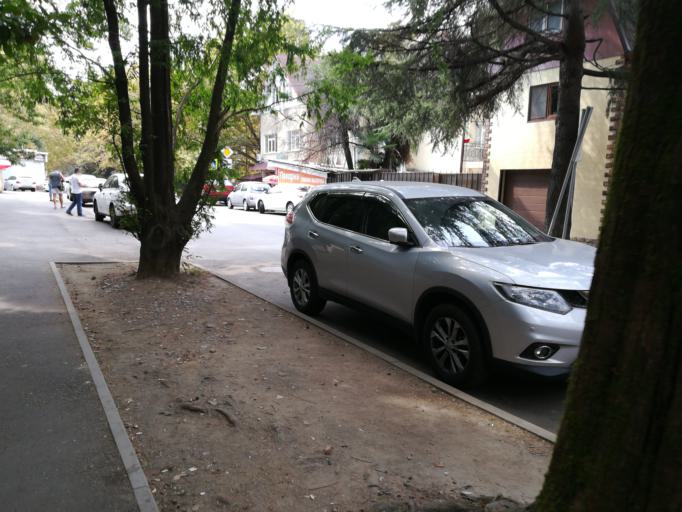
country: RU
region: Krasnodarskiy
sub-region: Sochi City
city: Sochi
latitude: 43.5930
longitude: 39.7386
